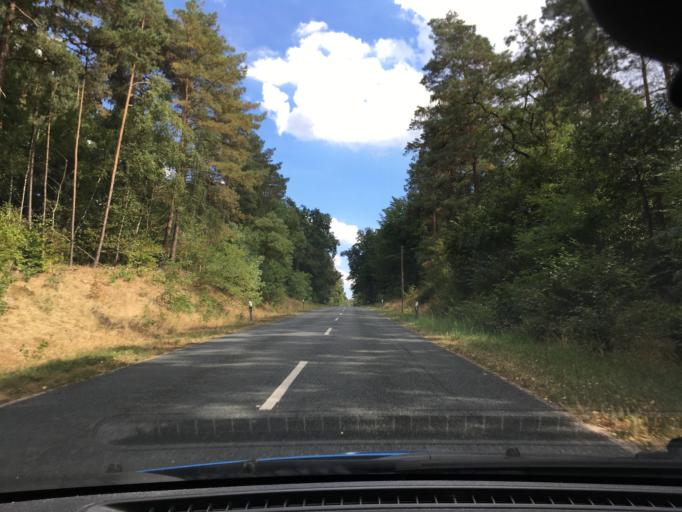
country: DE
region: Lower Saxony
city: Rehlingen
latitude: 53.0848
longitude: 10.2103
